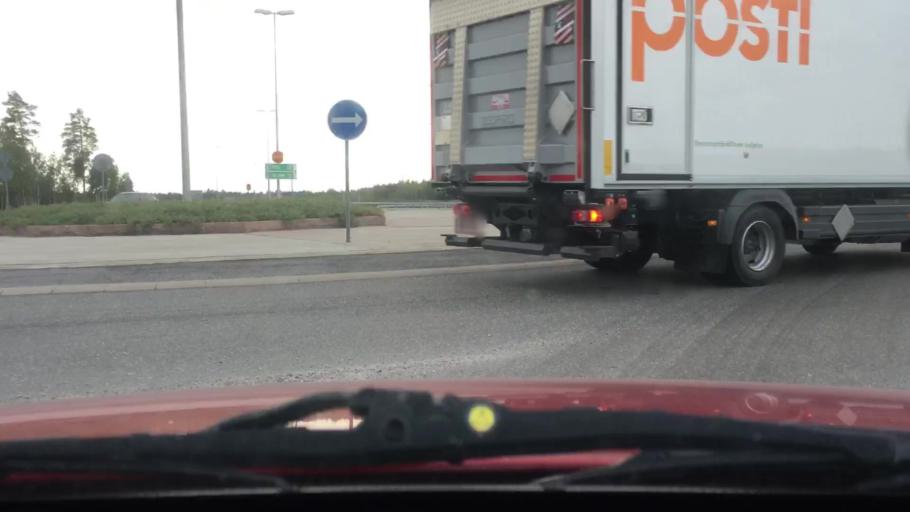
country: FI
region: Varsinais-Suomi
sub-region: Turku
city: Masku
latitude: 60.5427
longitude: 22.1287
